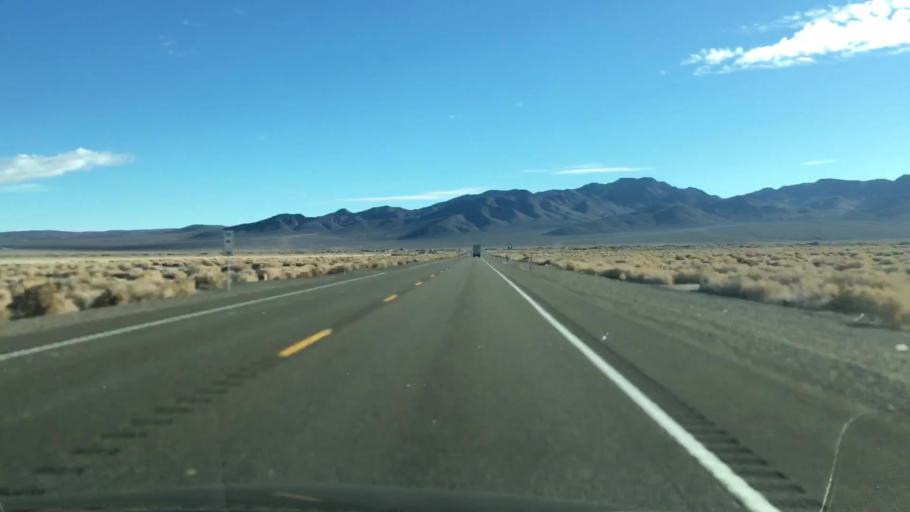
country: US
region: Nevada
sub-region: Mineral County
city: Hawthorne
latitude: 38.2793
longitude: -118.1001
